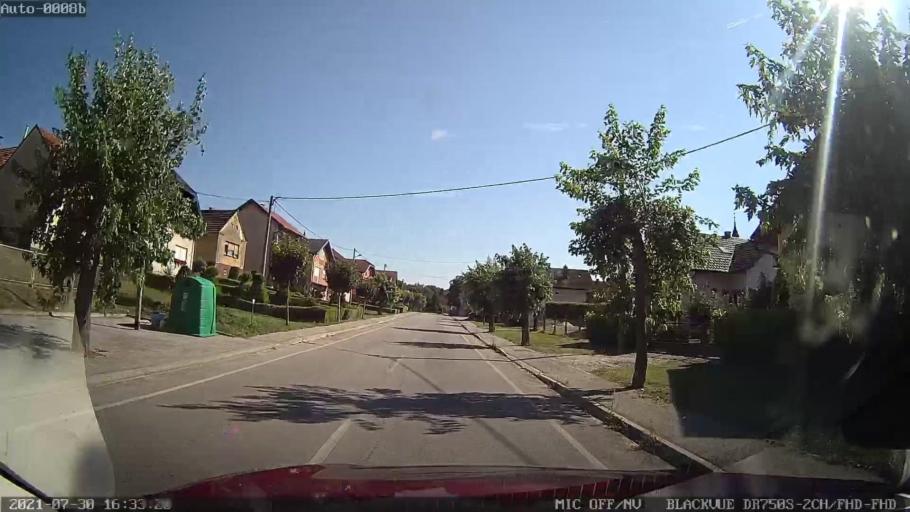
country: HR
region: Varazdinska
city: Jalzabet
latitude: 46.2591
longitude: 16.4742
